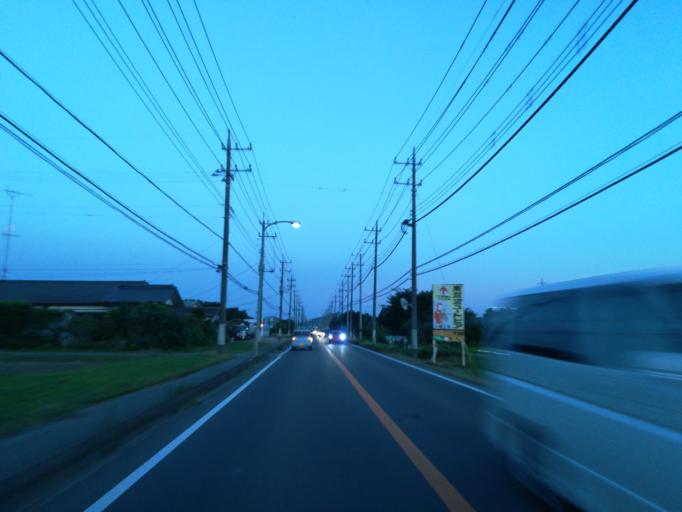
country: JP
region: Ibaraki
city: Tsukuba
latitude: 36.2128
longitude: 140.0698
